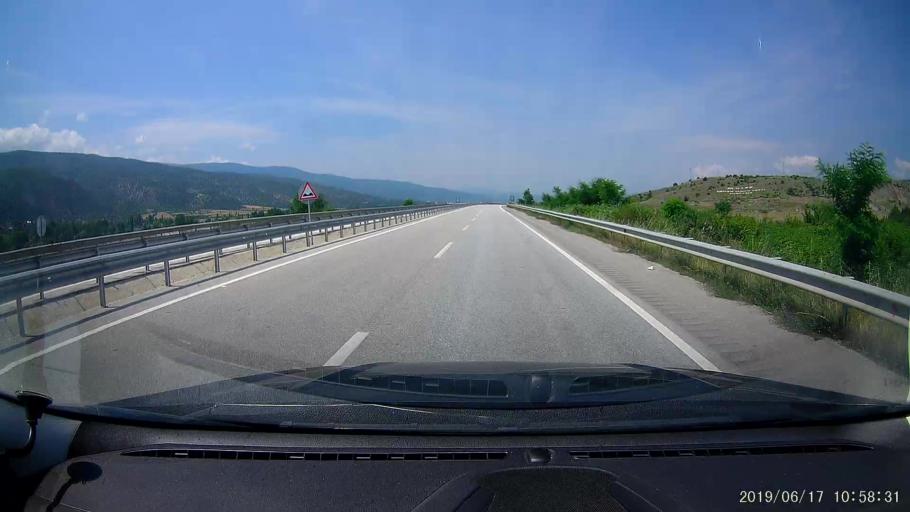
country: TR
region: Kastamonu
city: Tosya
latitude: 41.0421
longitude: 34.2228
